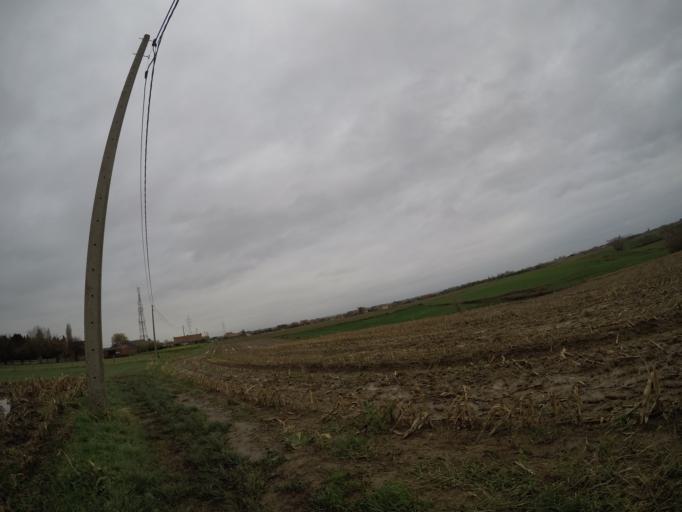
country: BE
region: Flanders
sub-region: Provincie West-Vlaanderen
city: Saint-Yvon
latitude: 50.7811
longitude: 2.8810
